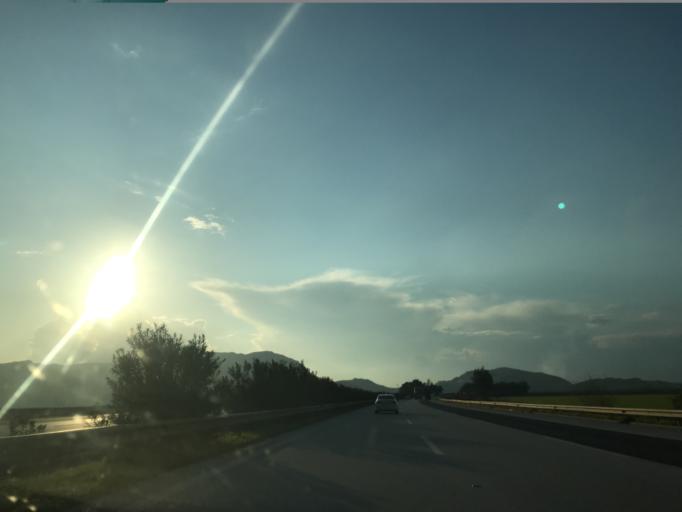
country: TR
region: Adana
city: Ceyhan
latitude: 36.9821
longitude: 35.7823
